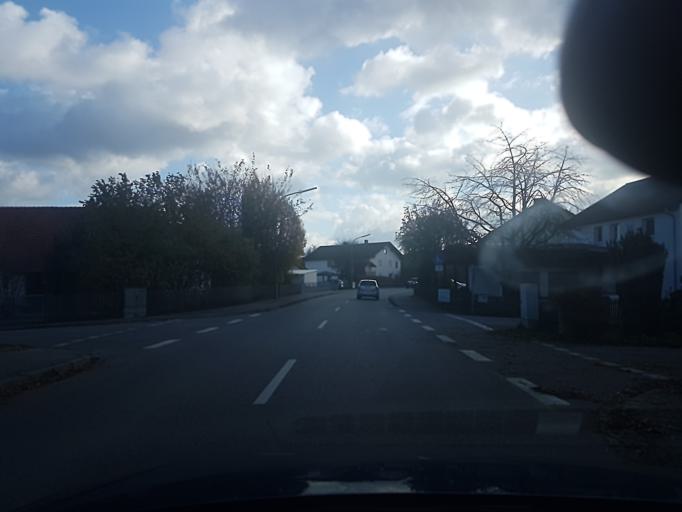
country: DE
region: Bavaria
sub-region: Lower Bavaria
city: Niederaichbach
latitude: 48.6107
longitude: 12.3172
